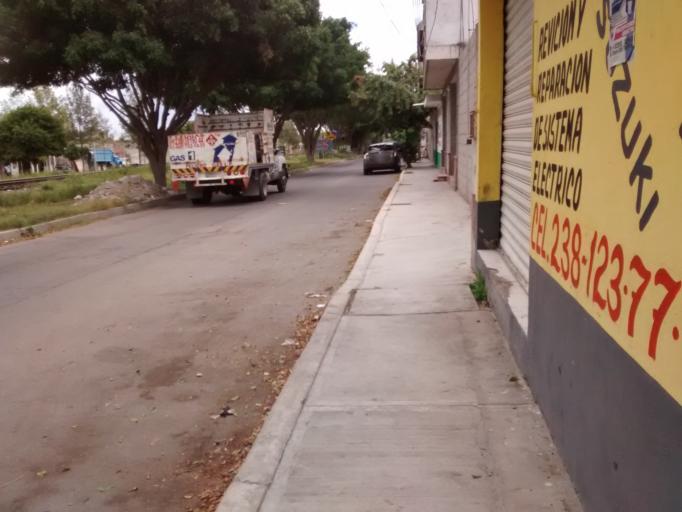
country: MX
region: Puebla
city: Tehuacan
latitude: 18.4741
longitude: -97.4077
